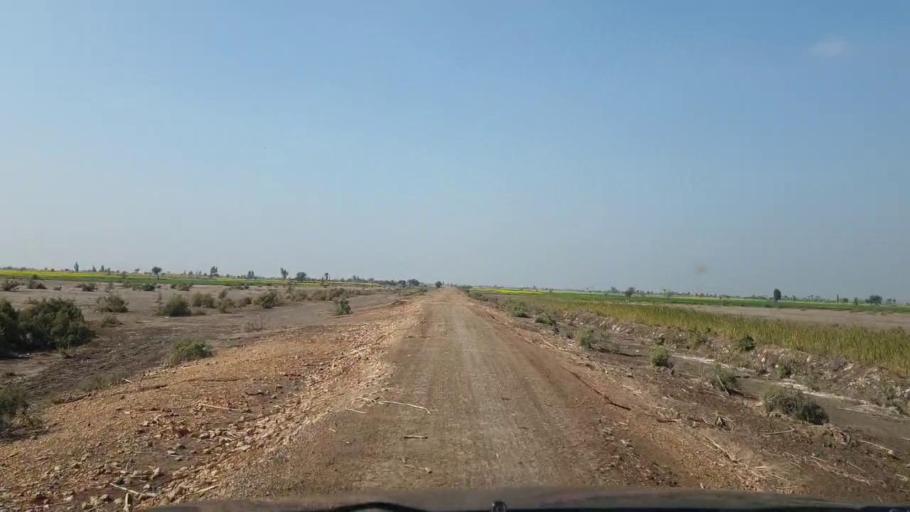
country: PK
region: Sindh
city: Sinjhoro
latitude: 26.0462
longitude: 68.7572
